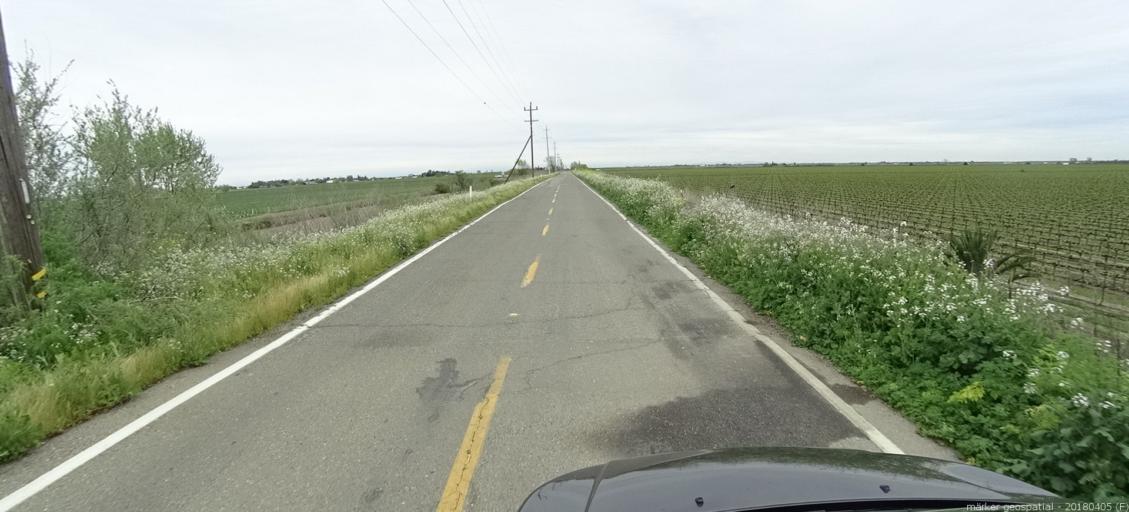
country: US
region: California
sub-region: Sacramento County
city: Walnut Grove
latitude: 38.3205
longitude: -121.4858
